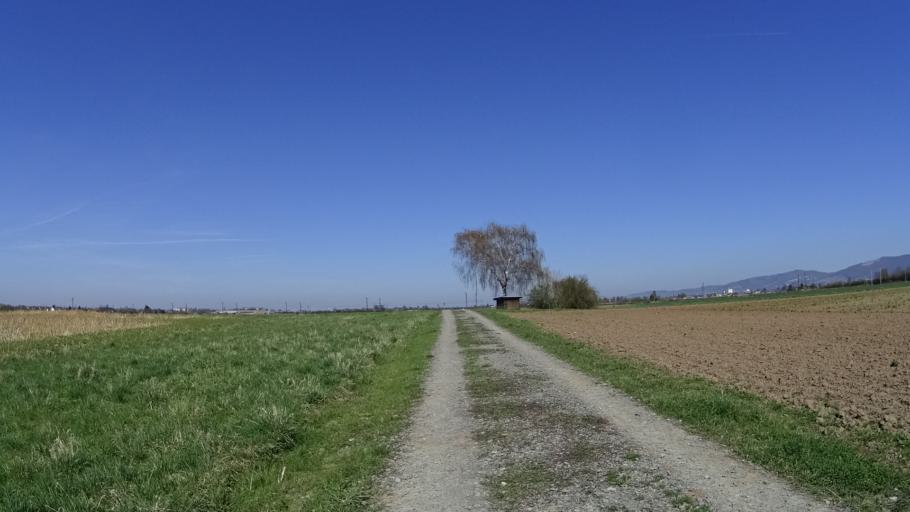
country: DE
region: Baden-Wuerttemberg
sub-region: Karlsruhe Region
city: Plankstadt
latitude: 49.4260
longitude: 8.5943
